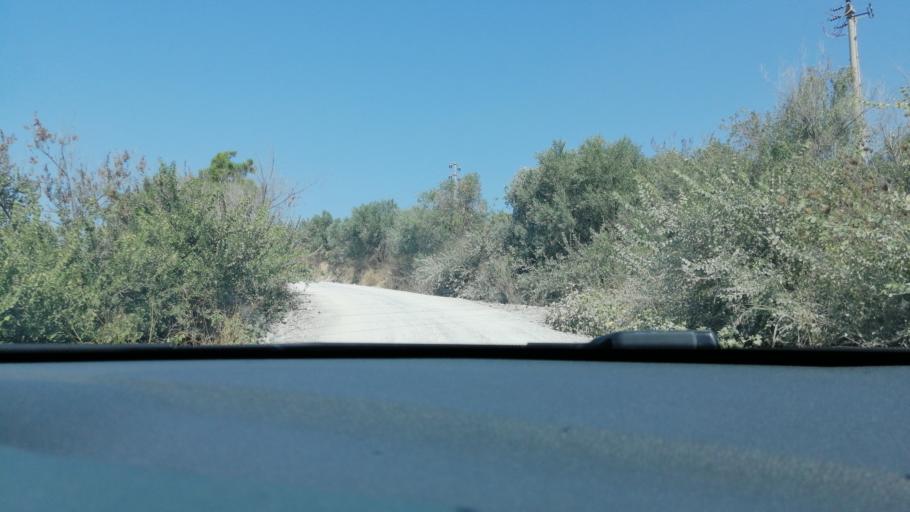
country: TR
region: Aydin
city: Davutlar
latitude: 37.7855
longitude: 27.3156
